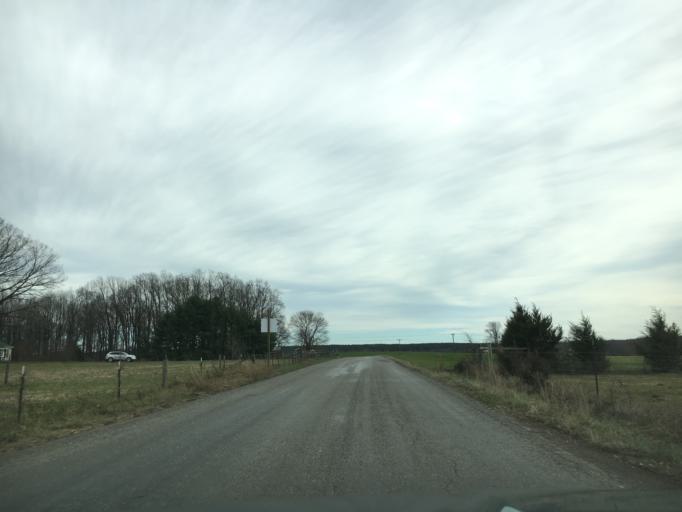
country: US
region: Virginia
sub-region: Amelia County
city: Amelia Court House
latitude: 37.4046
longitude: -77.9752
